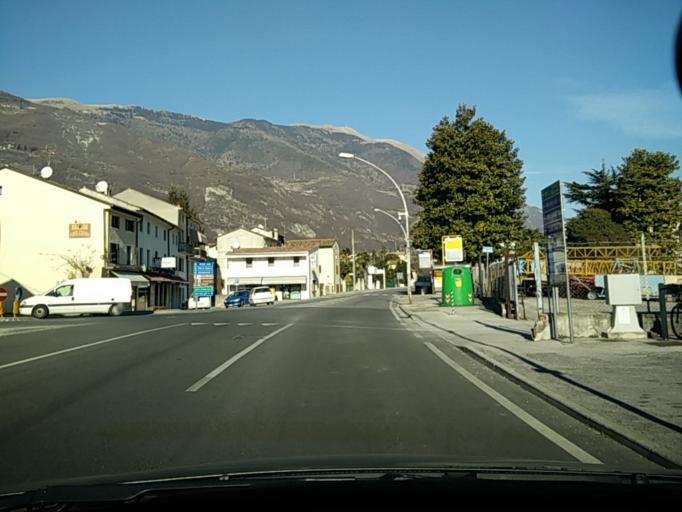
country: IT
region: Veneto
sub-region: Provincia di Treviso
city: Revine
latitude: 46.0062
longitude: 12.2859
